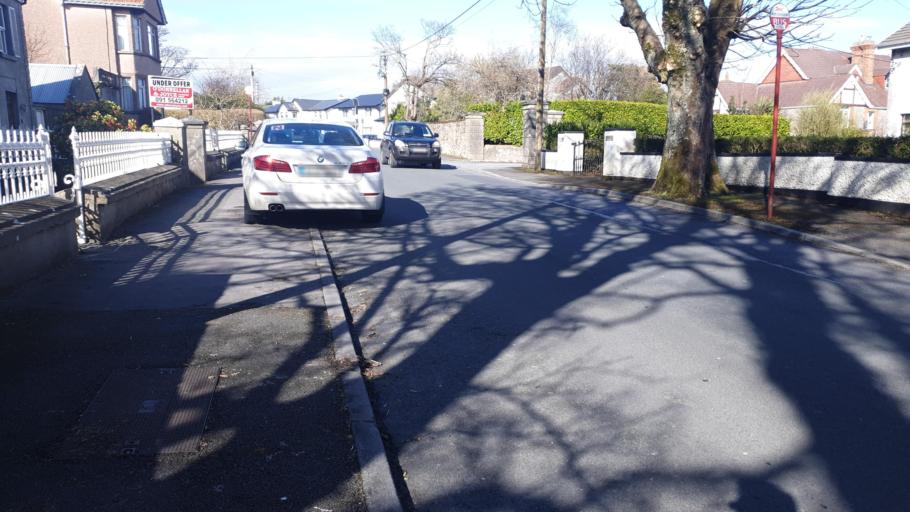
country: IE
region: Connaught
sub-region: County Galway
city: Gaillimh
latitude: 53.2701
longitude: -9.0718
